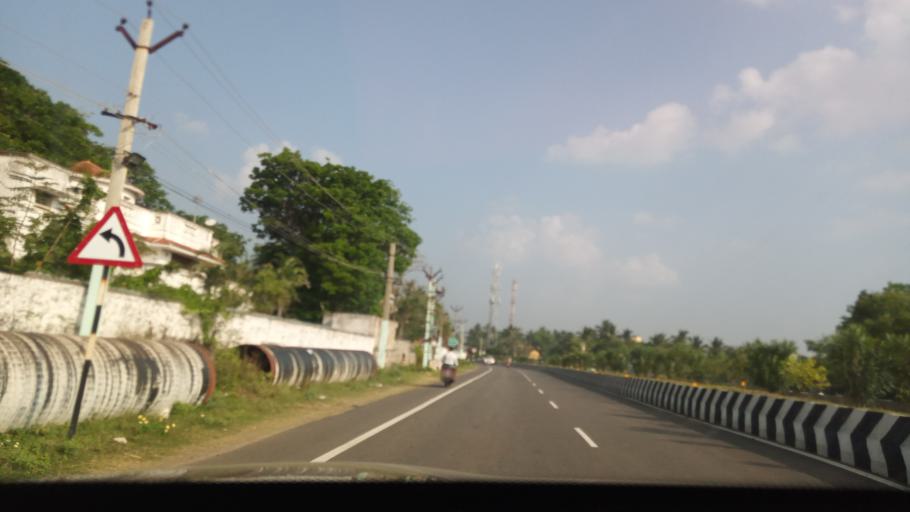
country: IN
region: Tamil Nadu
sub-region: Kancheepuram
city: Injambakkam
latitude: 12.7757
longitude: 80.2488
